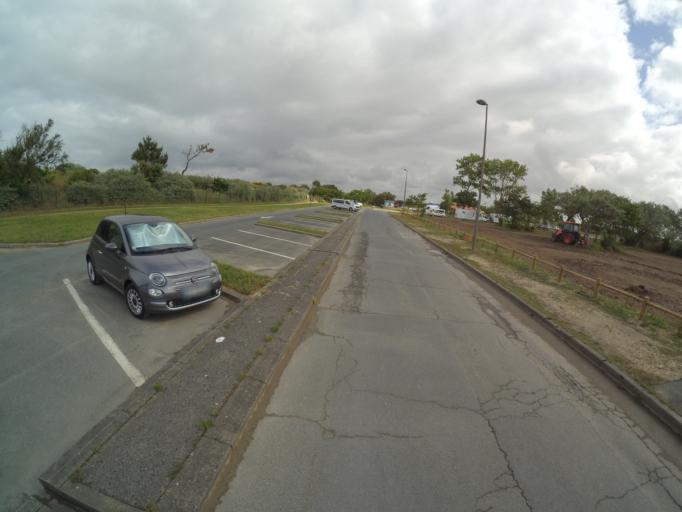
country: FR
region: Poitou-Charentes
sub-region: Departement de la Charente-Maritime
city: Angoulins
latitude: 46.1152
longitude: -1.1233
